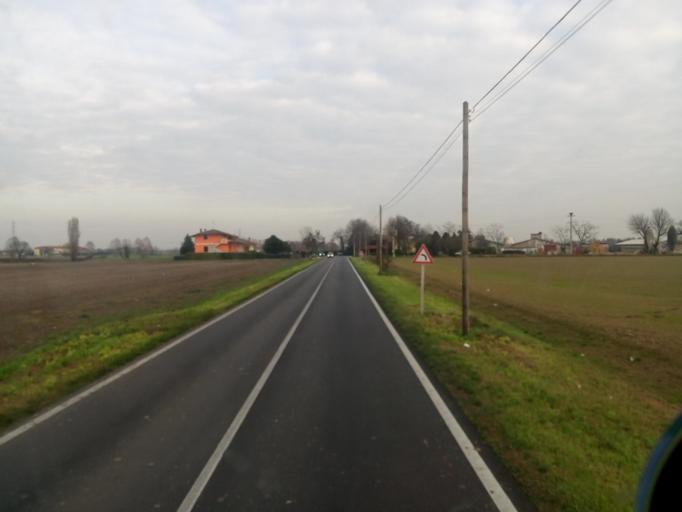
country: IT
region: Veneto
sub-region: Provincia di Verona
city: Nogarole Rocca
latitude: 45.2937
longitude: 10.9073
